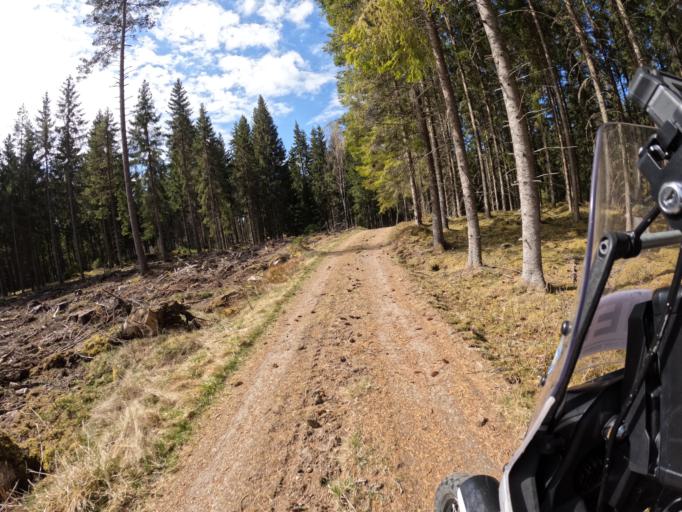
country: SE
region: Joenkoeping
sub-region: Mullsjo Kommun
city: Mullsjoe
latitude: 57.9463
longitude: 13.7003
